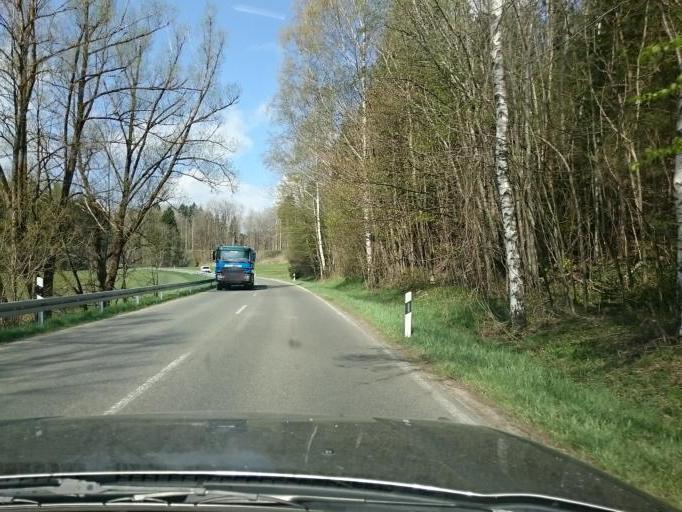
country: DE
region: Bavaria
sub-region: Upper Bavaria
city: Uffing
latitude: 47.6686
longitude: 11.1112
